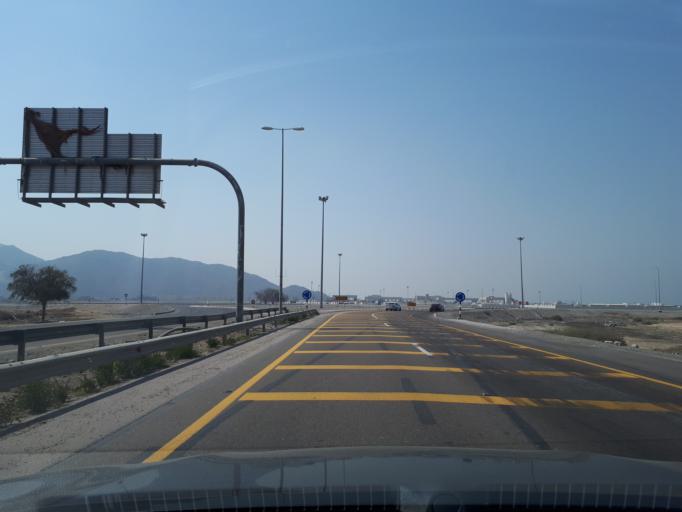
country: AE
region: Al Fujayrah
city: Al Fujayrah
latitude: 24.9646
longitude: 56.3690
